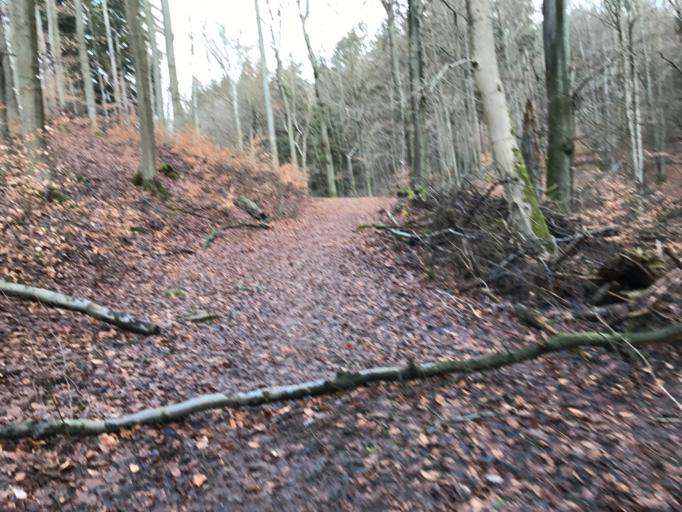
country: DE
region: Hesse
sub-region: Regierungsbezirk Darmstadt
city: Konigstein im Taunus
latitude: 50.2078
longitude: 8.4587
